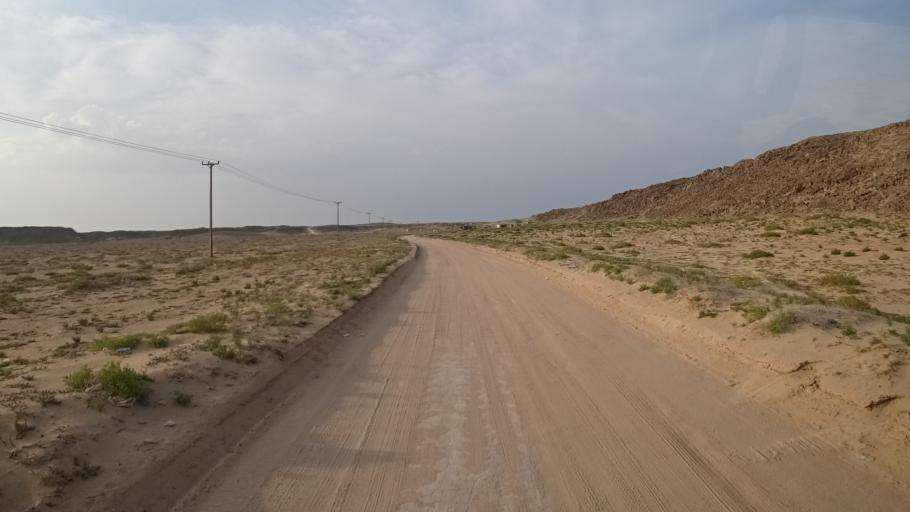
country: OM
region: Ash Sharqiyah
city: Sur
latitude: 22.4435
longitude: 59.8271
